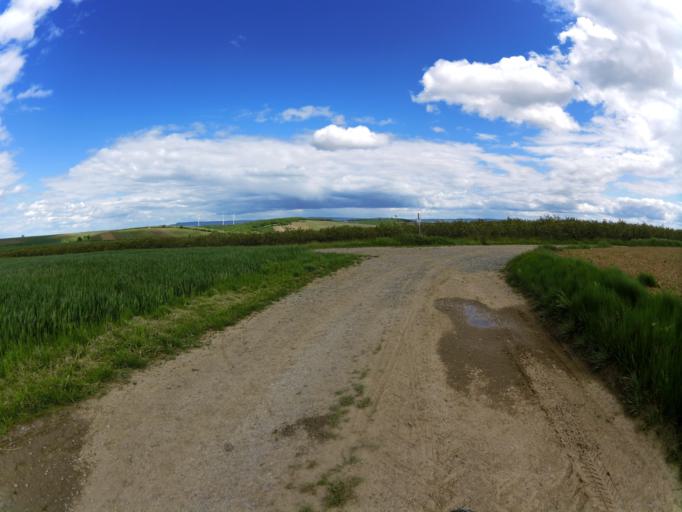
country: DE
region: Bavaria
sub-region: Regierungsbezirk Unterfranken
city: Volkach
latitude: 49.8786
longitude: 10.2317
